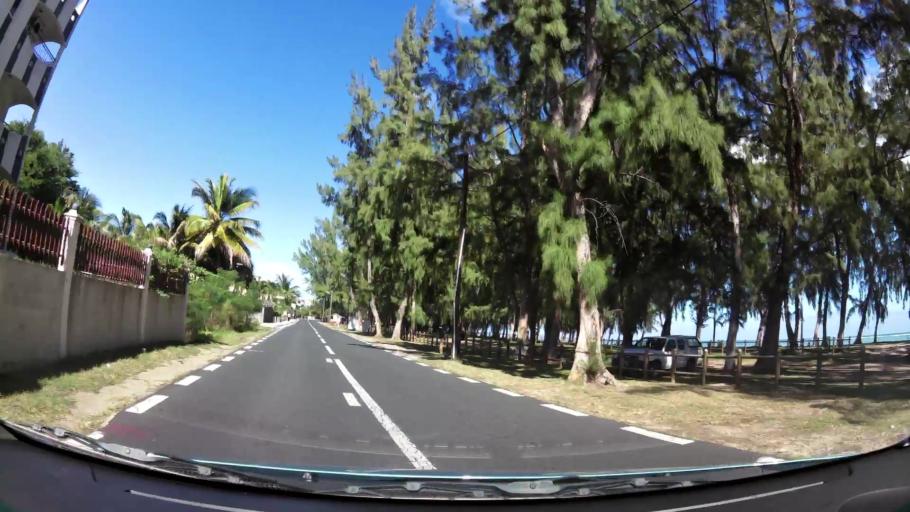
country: MU
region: Black River
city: Flic en Flac
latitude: -20.2901
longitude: 57.3637
